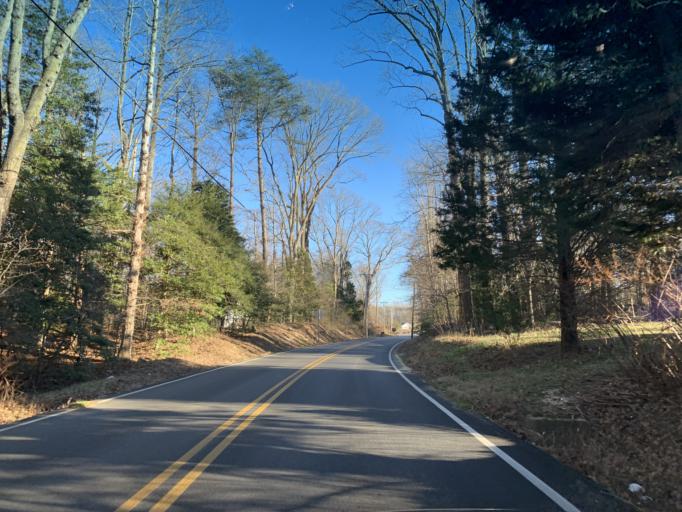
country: US
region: Maryland
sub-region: Saint Mary's County
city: Golden Beach
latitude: 38.4622
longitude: -76.6960
